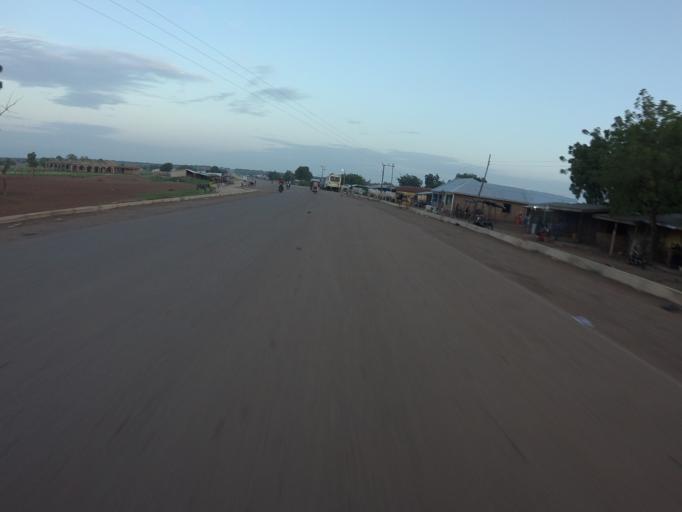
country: GH
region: Northern
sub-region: Yendi
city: Yendi
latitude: 9.9183
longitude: -0.2163
